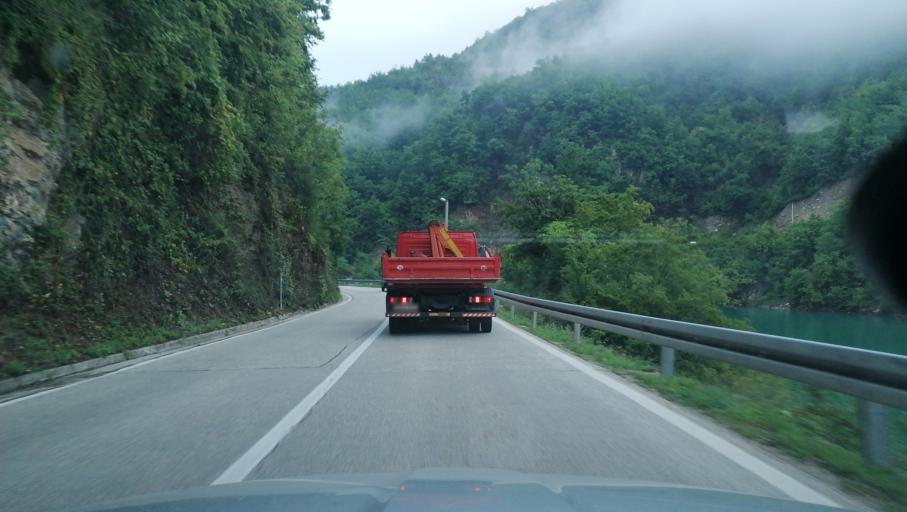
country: BA
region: Federation of Bosnia and Herzegovina
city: Jablanica
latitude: 43.7294
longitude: 17.6867
